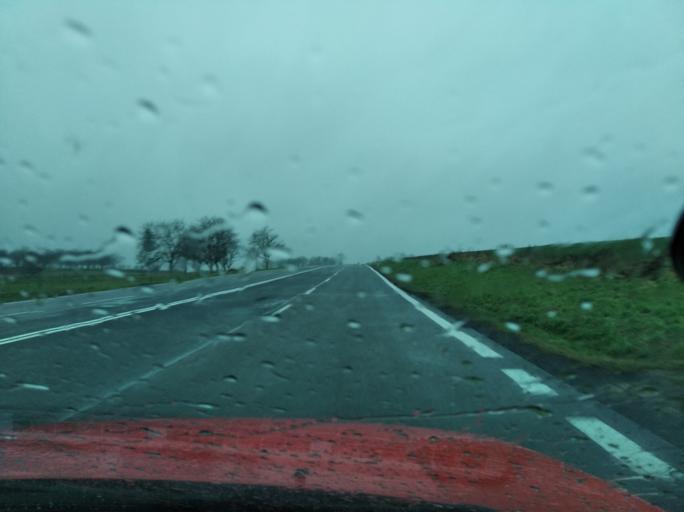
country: PL
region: Subcarpathian Voivodeship
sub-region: Powiat przeworski
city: Nowosielce
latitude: 50.0656
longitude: 22.4103
